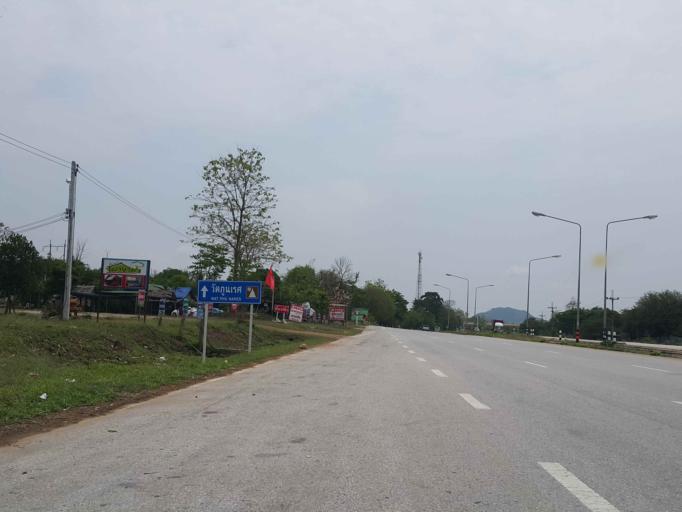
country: TH
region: Lampang
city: Thoen
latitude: 17.7354
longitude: 99.2334
